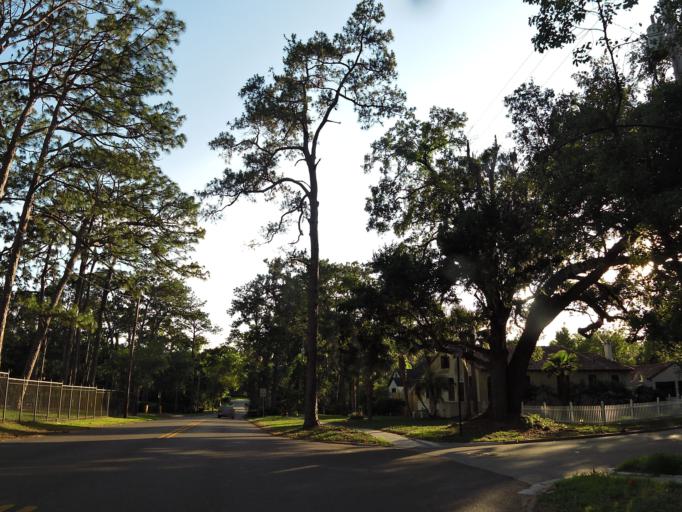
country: US
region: Florida
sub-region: Duval County
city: Jacksonville
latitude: 30.2993
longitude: -81.7122
